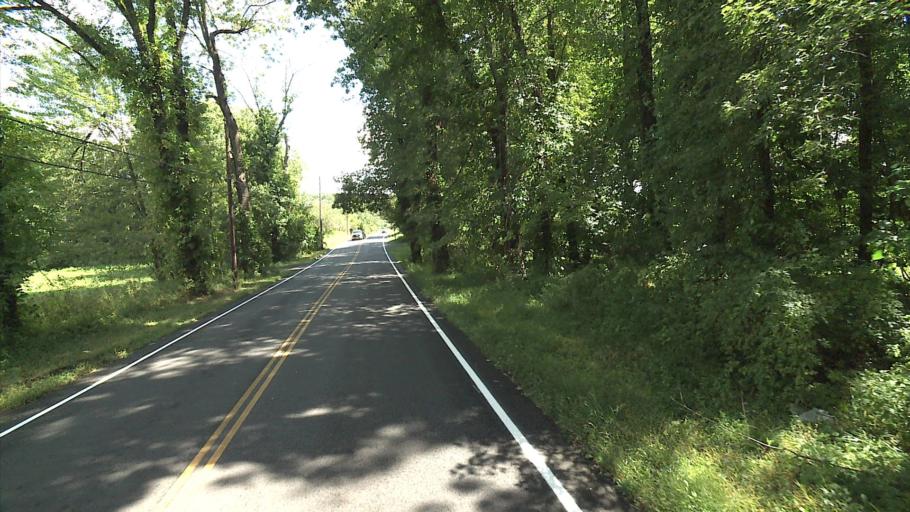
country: US
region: Connecticut
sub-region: Middlesex County
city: Cromwell
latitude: 41.6025
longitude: -72.6084
